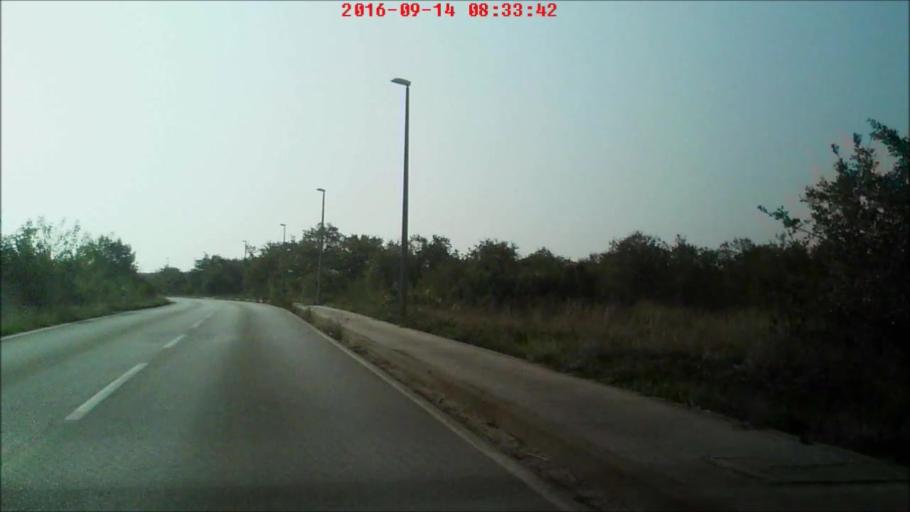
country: HR
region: Zadarska
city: Policnik
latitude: 44.1546
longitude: 15.3139
